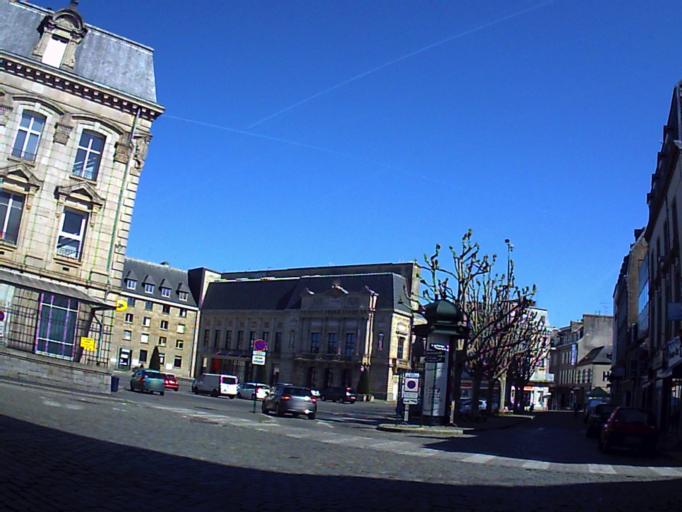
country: FR
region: Brittany
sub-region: Departement des Cotes-d'Armor
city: Saint-Brieuc
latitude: 48.5129
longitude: -2.7614
